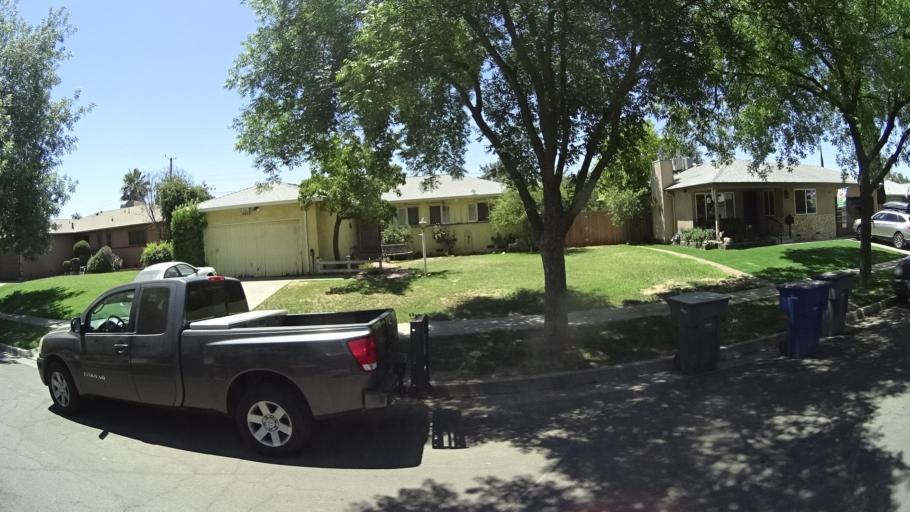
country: US
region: California
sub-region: Fresno County
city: Fresno
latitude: 36.8042
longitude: -119.7827
